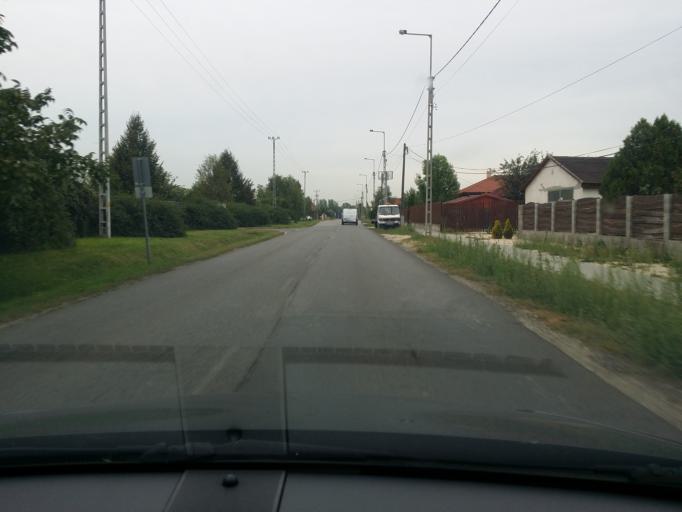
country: HU
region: Pest
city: Alsonemedi
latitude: 47.3238
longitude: 19.1485
